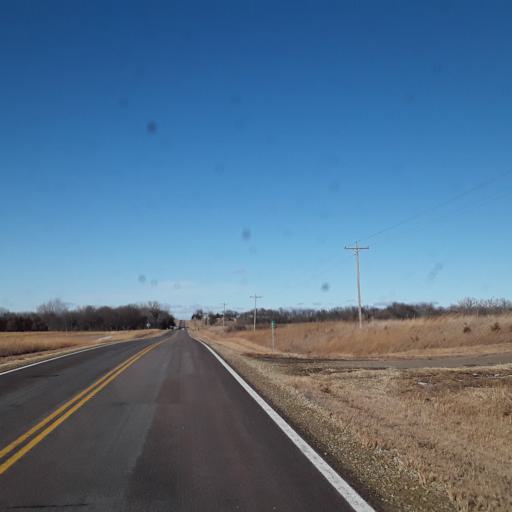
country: US
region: Kansas
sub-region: Cloud County
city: Concordia
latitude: 39.5005
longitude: -97.7228
